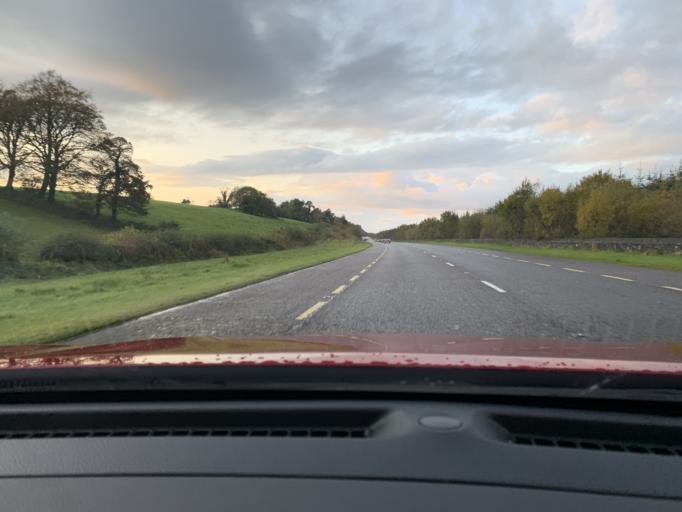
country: IE
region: Connaught
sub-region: Roscommon
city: Boyle
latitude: 54.0578
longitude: -8.3461
